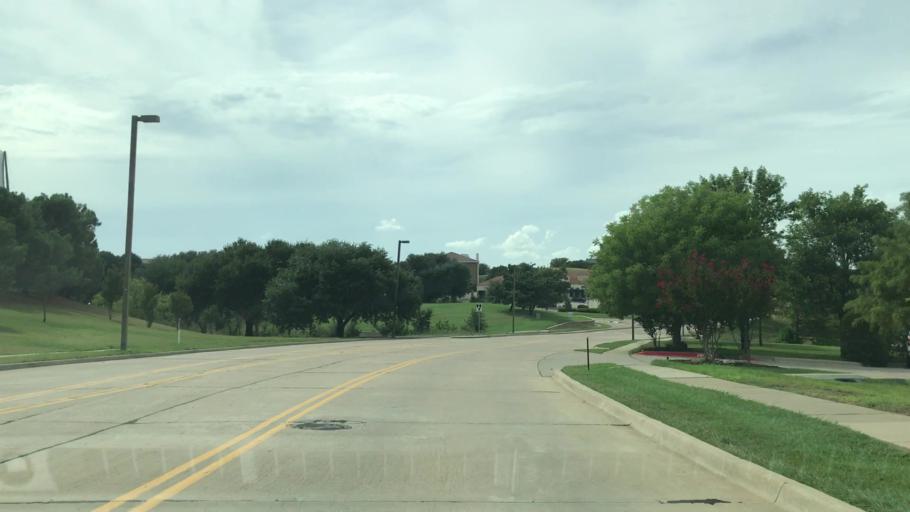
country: US
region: Texas
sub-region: Dallas County
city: Irving
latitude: 32.8642
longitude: -96.9467
